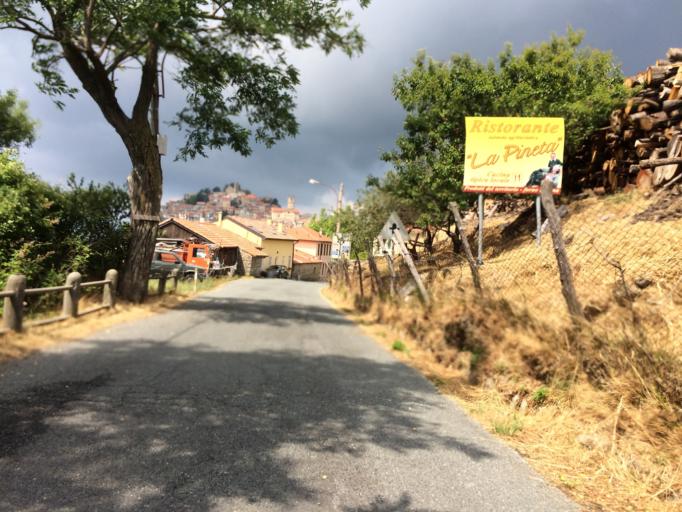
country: IT
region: Liguria
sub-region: Provincia di Imperia
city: Bajardo
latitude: 43.9032
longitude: 7.7231
